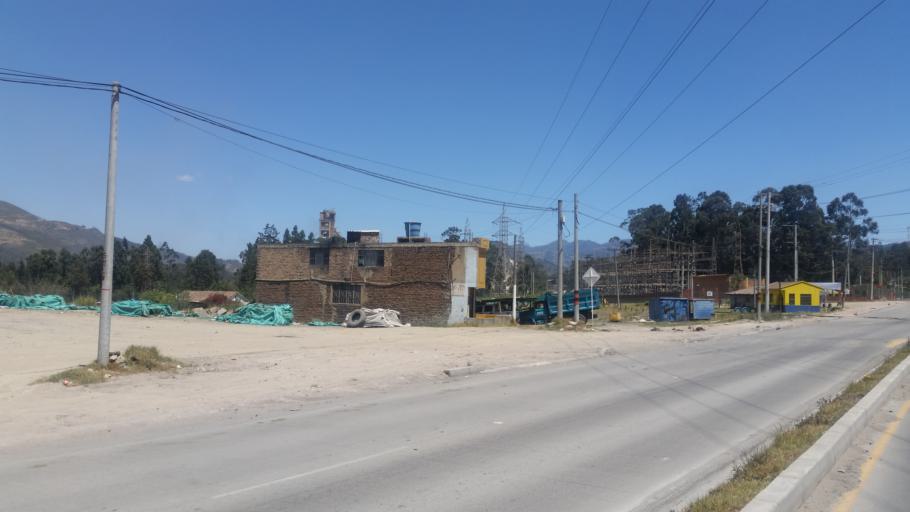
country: CO
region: Boyaca
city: Nobsa
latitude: 5.7579
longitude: -72.8945
